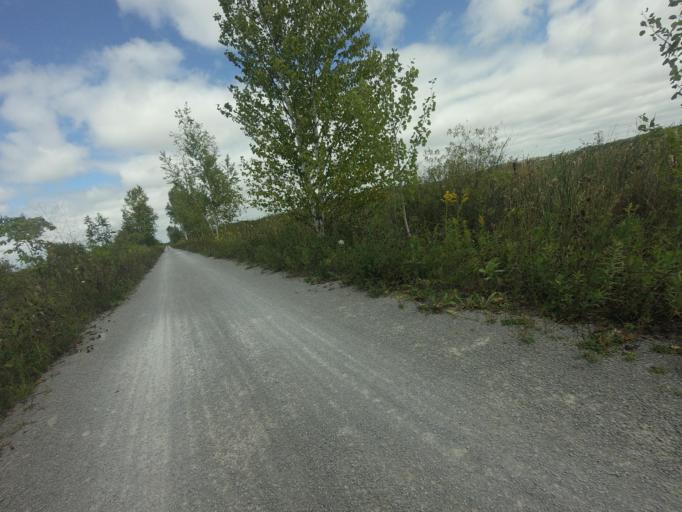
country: CA
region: Ontario
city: Uxbridge
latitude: 44.1560
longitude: -79.0817
